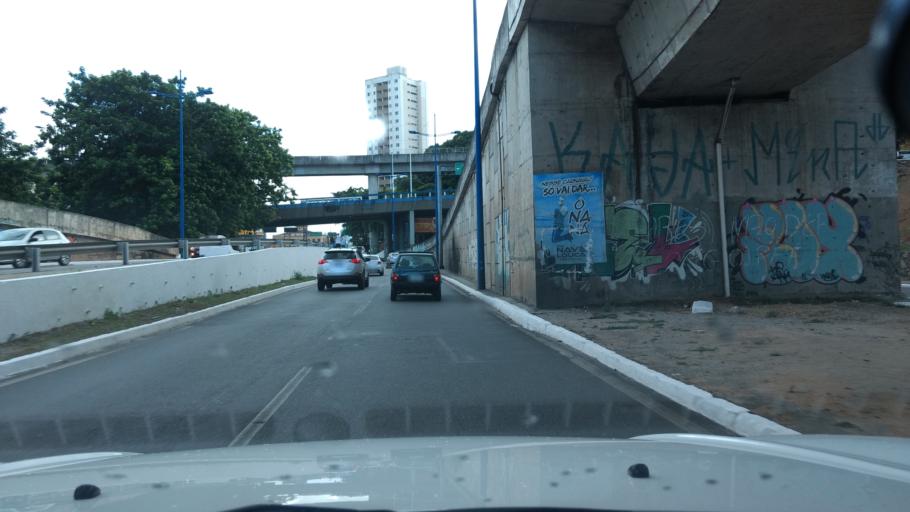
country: BR
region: Bahia
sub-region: Salvador
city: Salvador
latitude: -12.9788
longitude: -38.5023
